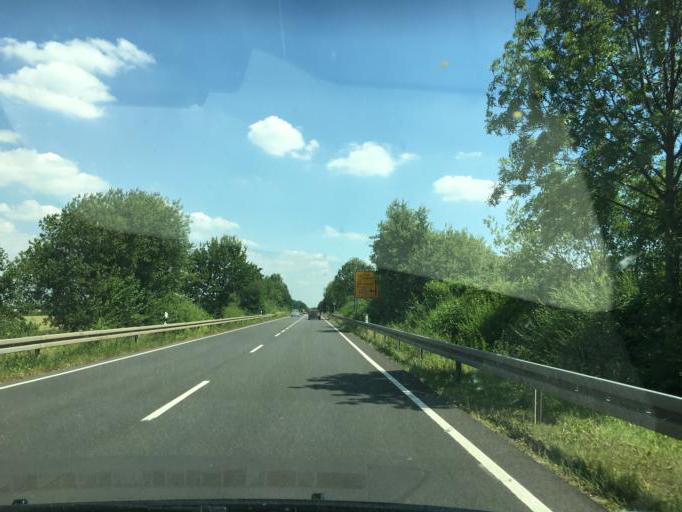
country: DE
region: North Rhine-Westphalia
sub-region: Regierungsbezirk Koln
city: Langerwehe
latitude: 50.8250
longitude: 6.3483
